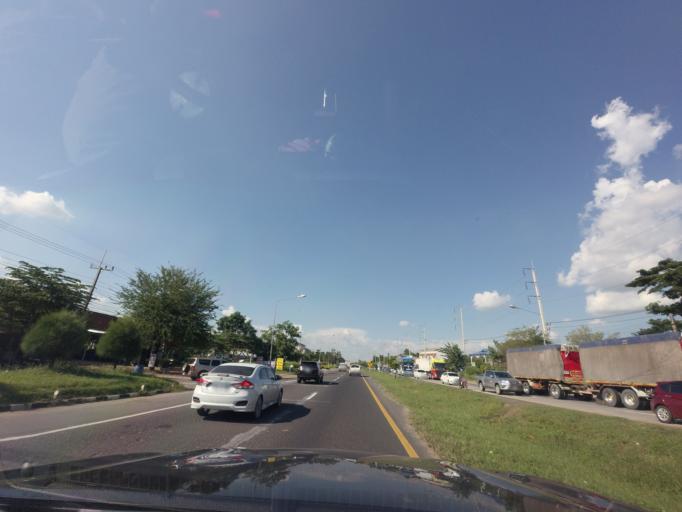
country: TH
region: Nakhon Ratchasima
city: Sida
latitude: 15.5490
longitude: 102.5483
